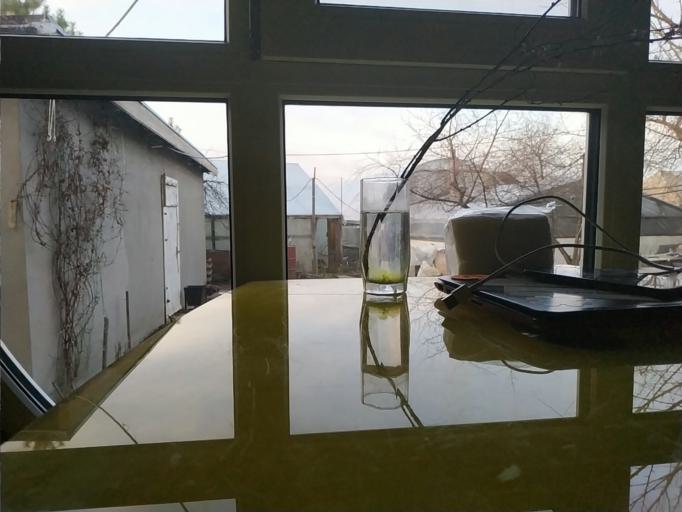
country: RU
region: Republic of Karelia
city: Suoyarvi
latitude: 62.3774
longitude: 32.0372
